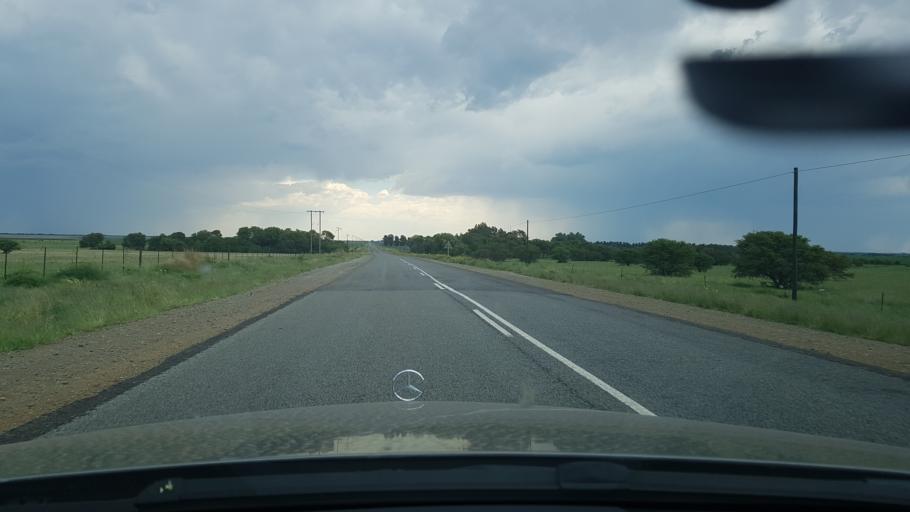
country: ZA
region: Orange Free State
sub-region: Lejweleputswa District Municipality
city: Hoopstad
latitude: -27.9555
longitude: 25.7028
